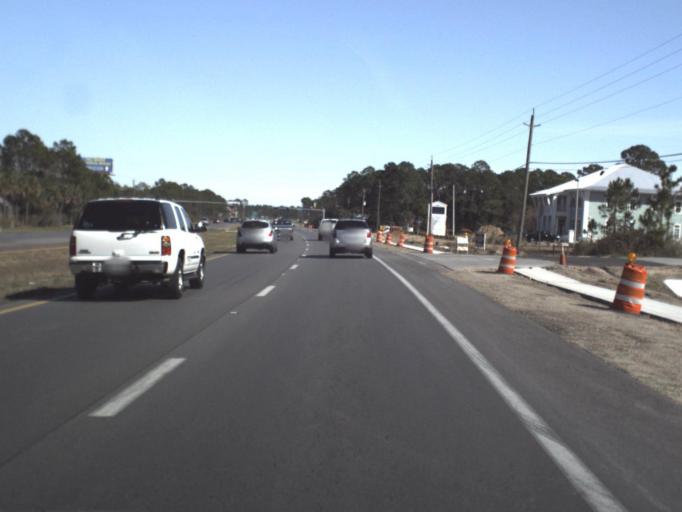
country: US
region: Florida
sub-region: Bay County
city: Panama City Beach
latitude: 30.2056
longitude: -85.8388
